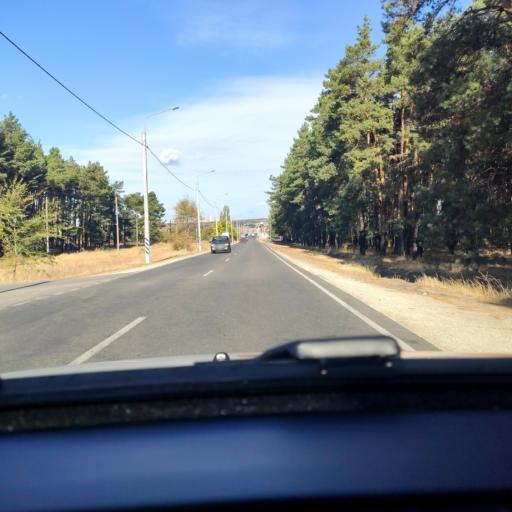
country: RU
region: Voronezj
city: Shilovo
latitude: 51.5341
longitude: 39.1398
